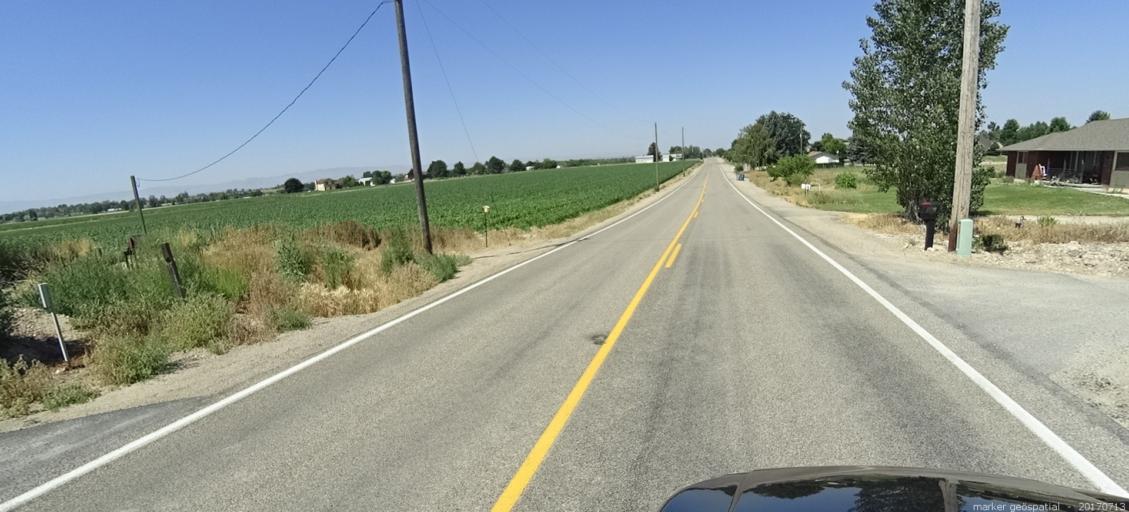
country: US
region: Idaho
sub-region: Ada County
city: Kuna
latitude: 43.5321
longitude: -116.4435
